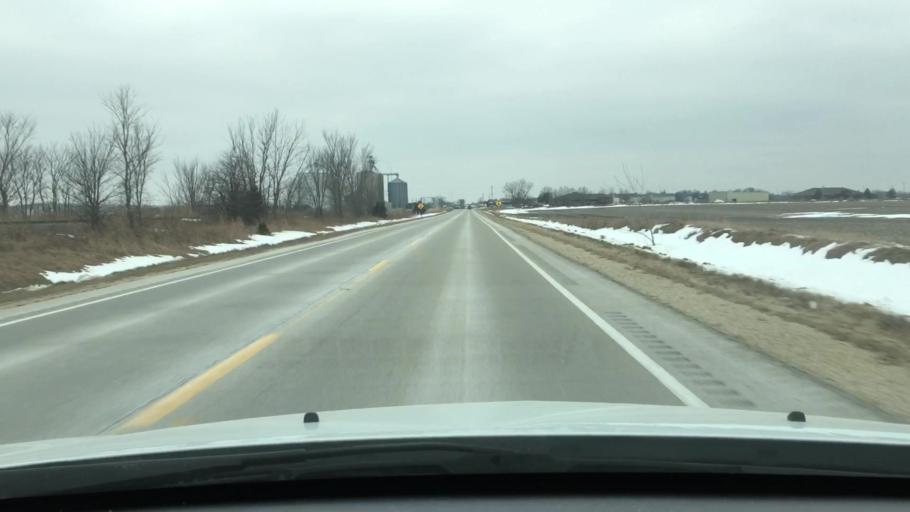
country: US
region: Illinois
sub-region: DeKalb County
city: Waterman
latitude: 41.7693
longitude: -88.7474
